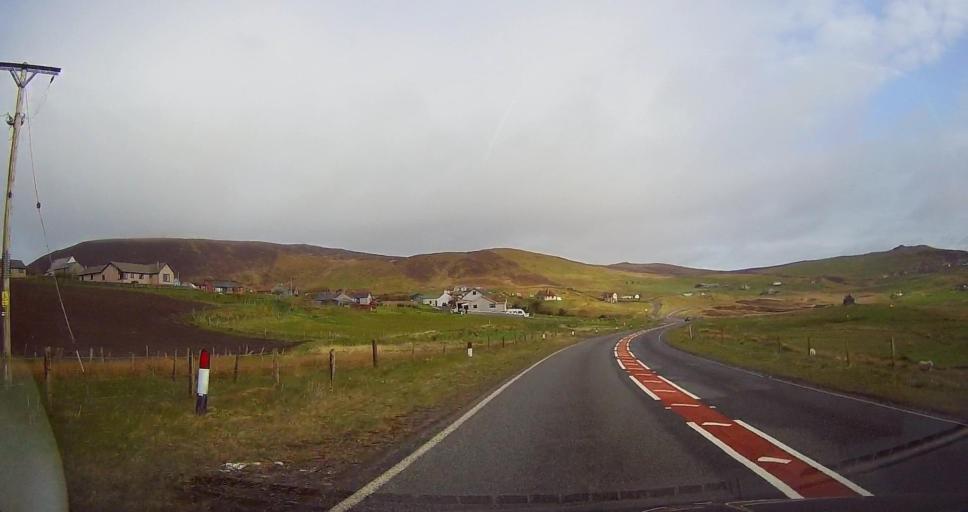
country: GB
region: Scotland
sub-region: Shetland Islands
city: Sandwick
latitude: 60.0964
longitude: -1.2339
